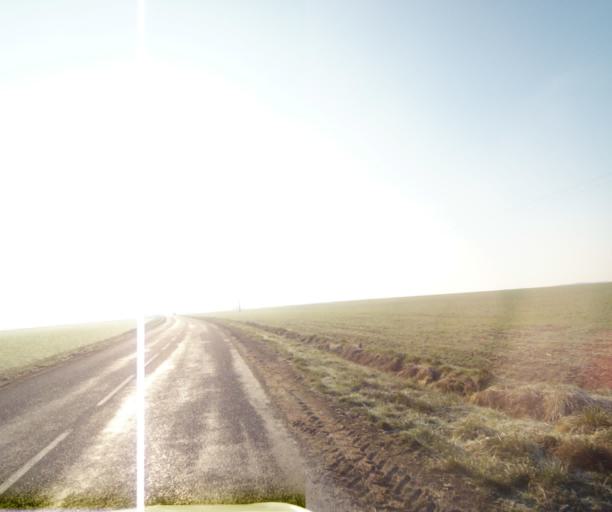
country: FR
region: Champagne-Ardenne
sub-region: Departement de la Haute-Marne
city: Montier-en-Der
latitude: 48.5007
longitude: 4.7508
